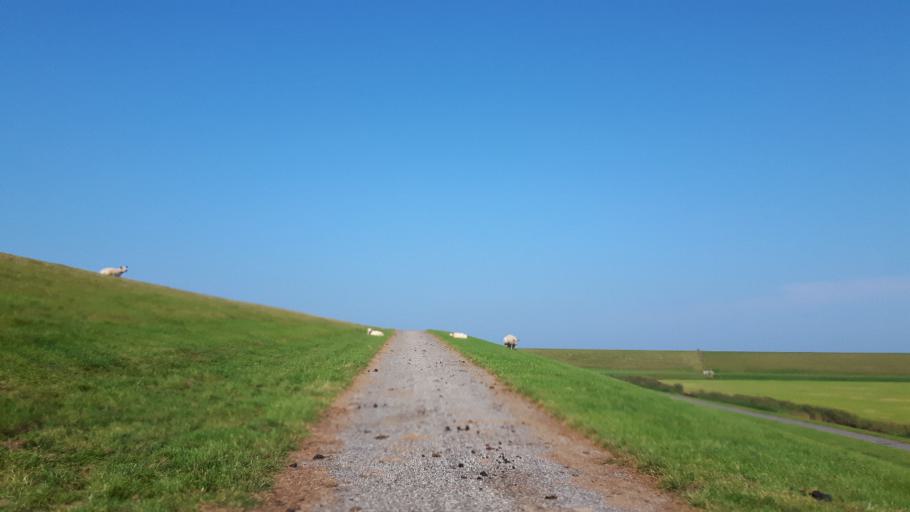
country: NL
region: Friesland
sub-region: Sudwest Fryslan
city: Makkum
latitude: 53.1057
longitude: 5.3825
